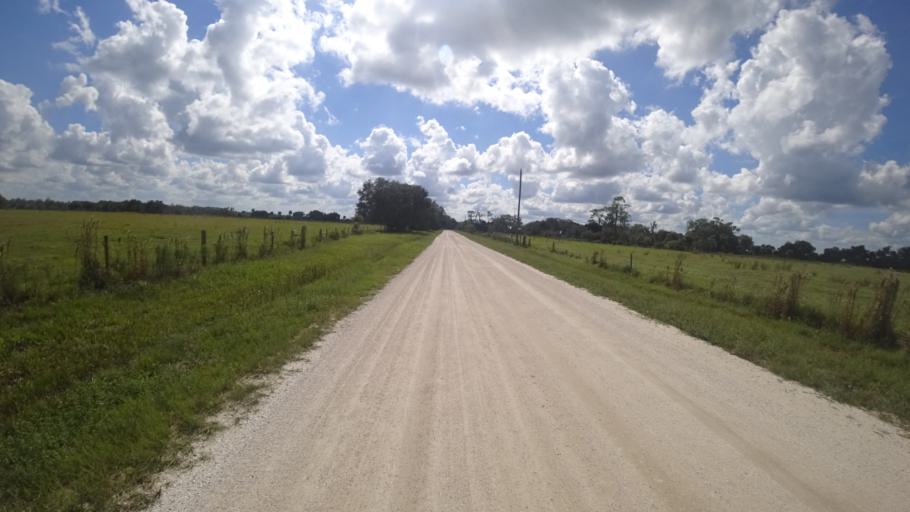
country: US
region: Florida
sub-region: Sarasota County
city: Warm Mineral Springs
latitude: 27.2635
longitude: -82.1570
